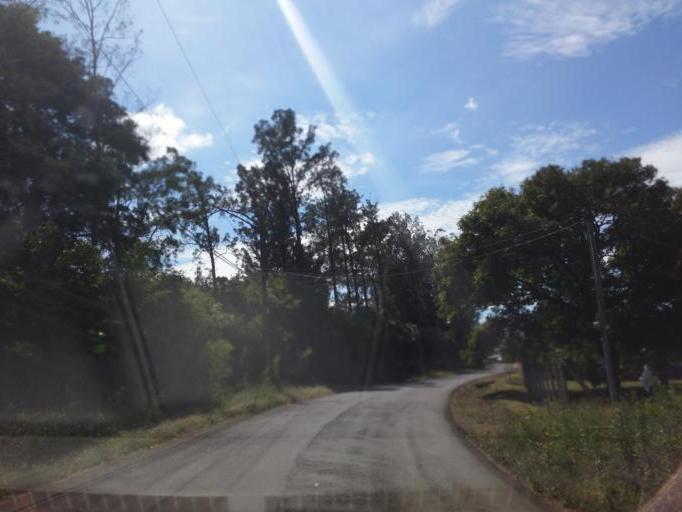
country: CR
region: Heredia
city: Santo Domingo
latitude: 10.0595
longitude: -84.1465
